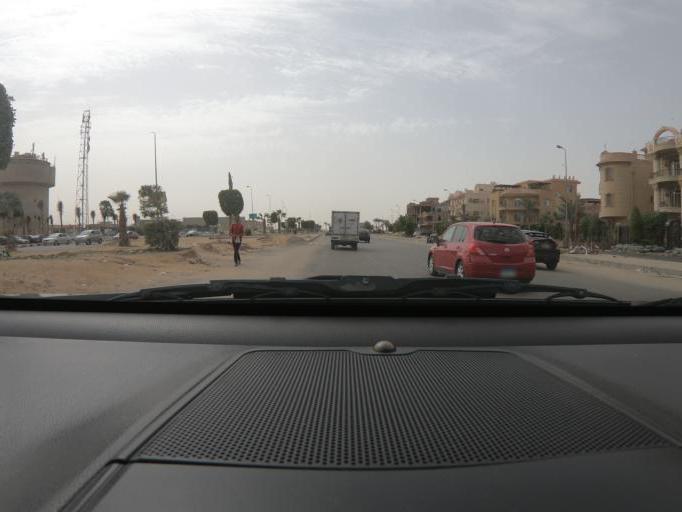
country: EG
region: Muhafazat al Qahirah
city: Cairo
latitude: 30.0215
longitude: 31.4145
